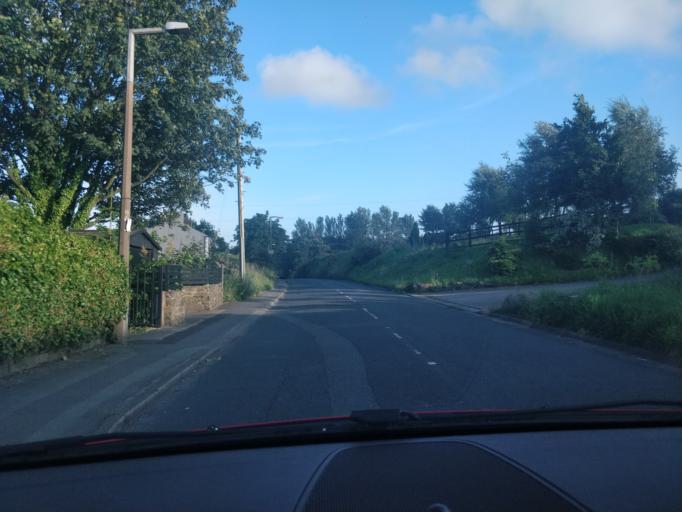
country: GB
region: England
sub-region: St. Helens
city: Billinge
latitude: 53.5365
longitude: -2.7210
